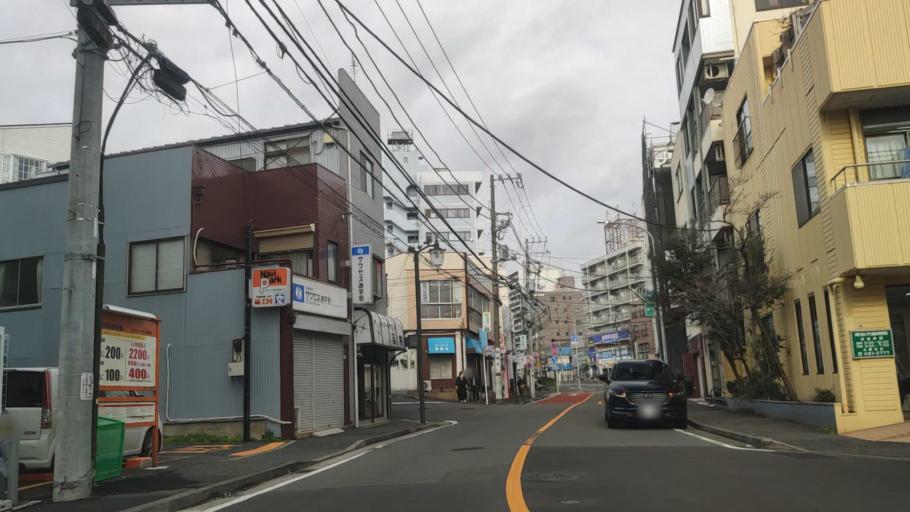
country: JP
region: Kanagawa
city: Yokohama
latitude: 35.4843
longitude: 139.6274
